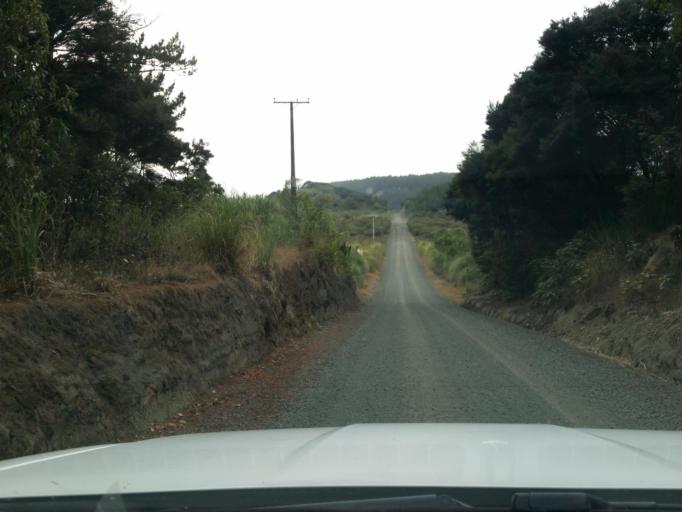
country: NZ
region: Northland
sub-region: Kaipara District
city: Dargaville
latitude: -36.2357
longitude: 174.0703
